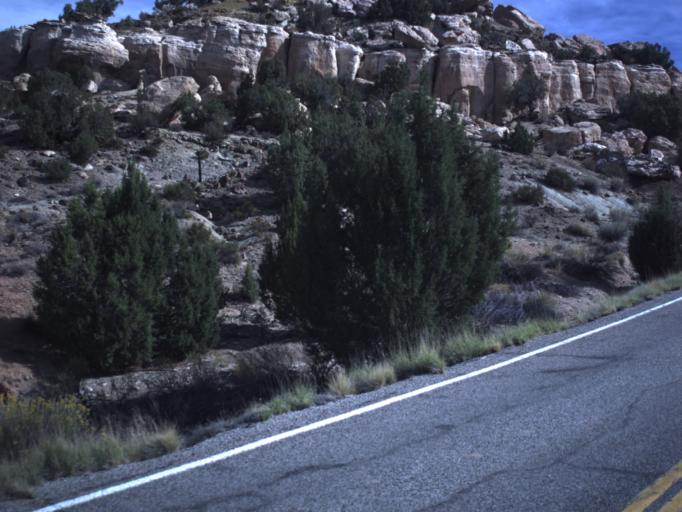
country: US
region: Utah
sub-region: San Juan County
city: Blanding
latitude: 37.4343
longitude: -109.3946
